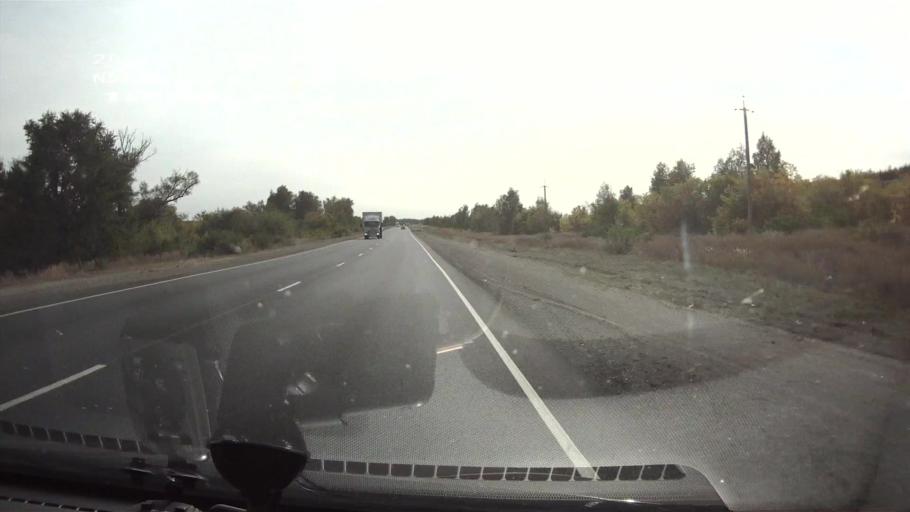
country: RU
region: Saratov
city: Sinodskoye
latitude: 52.0648
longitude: 46.7678
